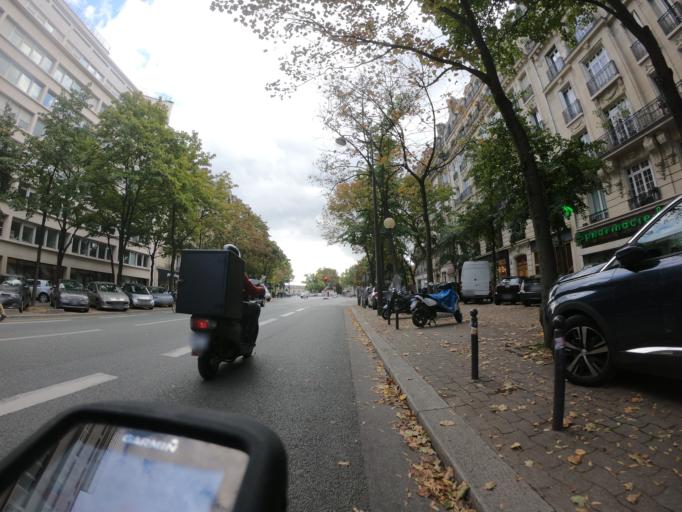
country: FR
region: Ile-de-France
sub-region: Paris
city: Paris
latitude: 48.8357
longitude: 2.3319
